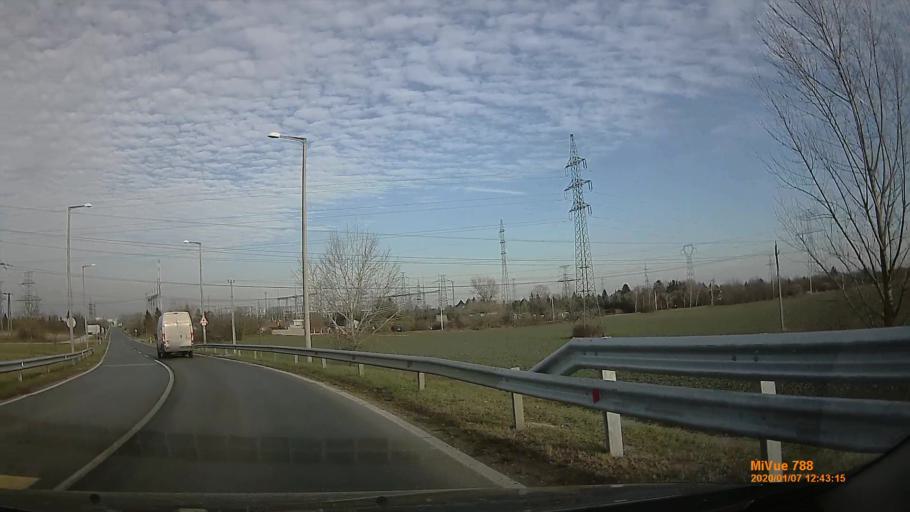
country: HU
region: Gyor-Moson-Sopron
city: Gyor
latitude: 47.6686
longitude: 17.6894
